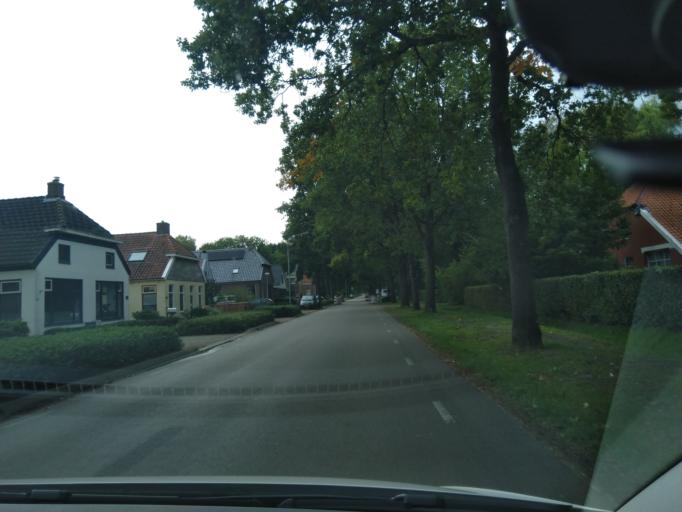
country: NL
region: Groningen
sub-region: Gemeente Veendam
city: Veendam
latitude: 53.0954
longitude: 6.9389
